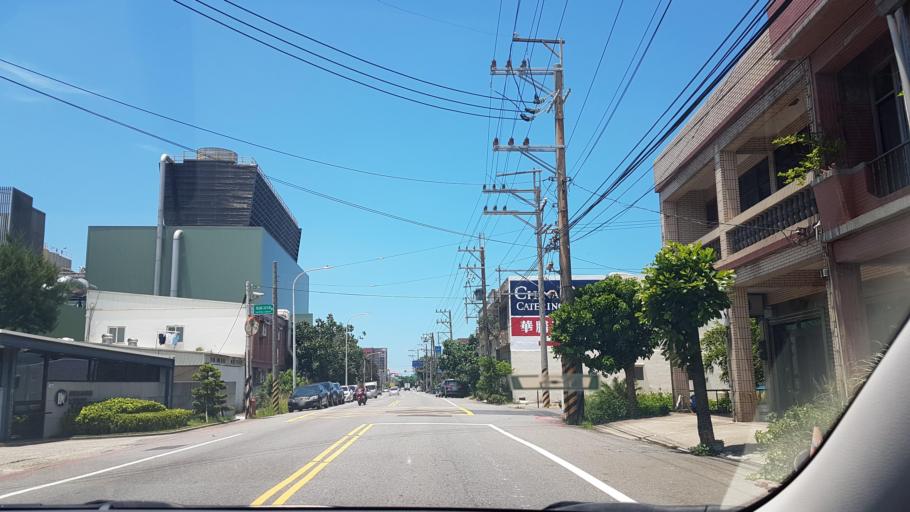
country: TW
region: Taiwan
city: Taoyuan City
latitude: 25.1032
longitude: 121.2597
